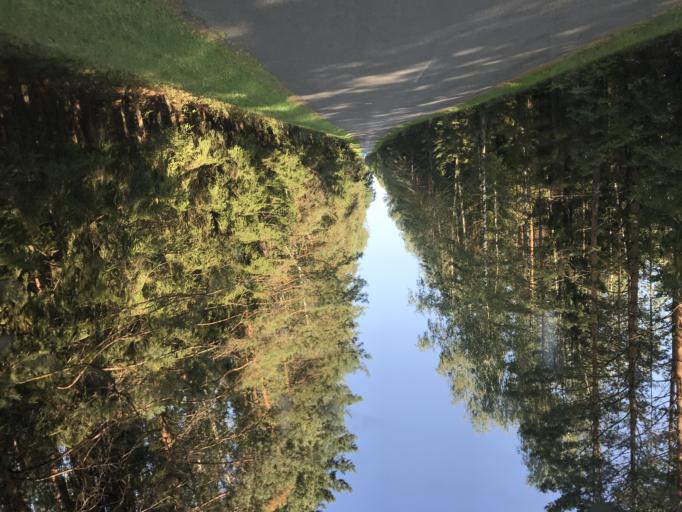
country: BY
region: Mogilev
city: Myazhysyatki
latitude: 53.7999
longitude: 30.1780
